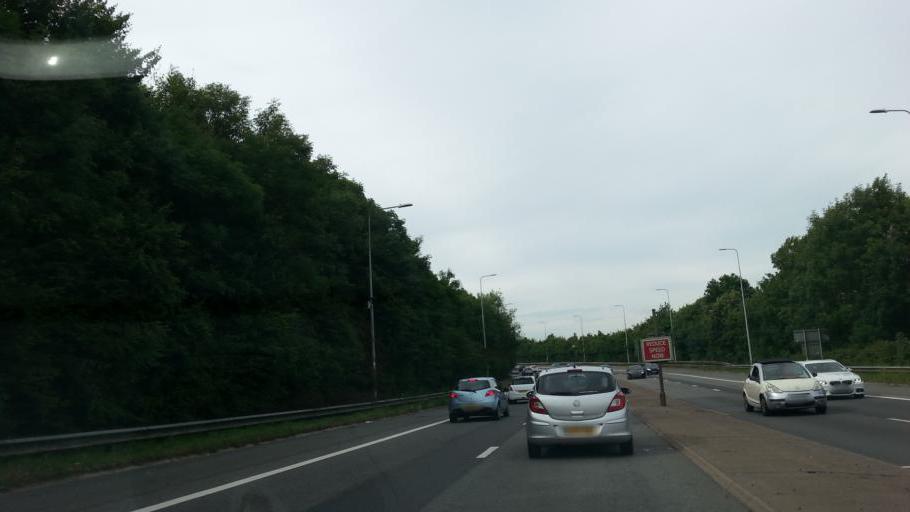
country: GB
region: Wales
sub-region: Cardiff
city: Cardiff
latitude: 51.5041
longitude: -3.1435
